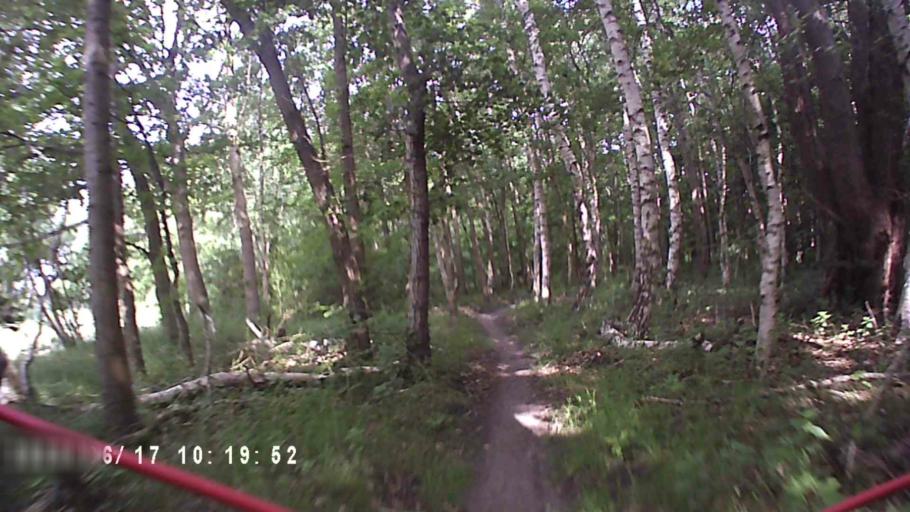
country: NL
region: Groningen
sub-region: Gemeente De Marne
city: Ulrum
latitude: 53.3887
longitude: 6.2492
